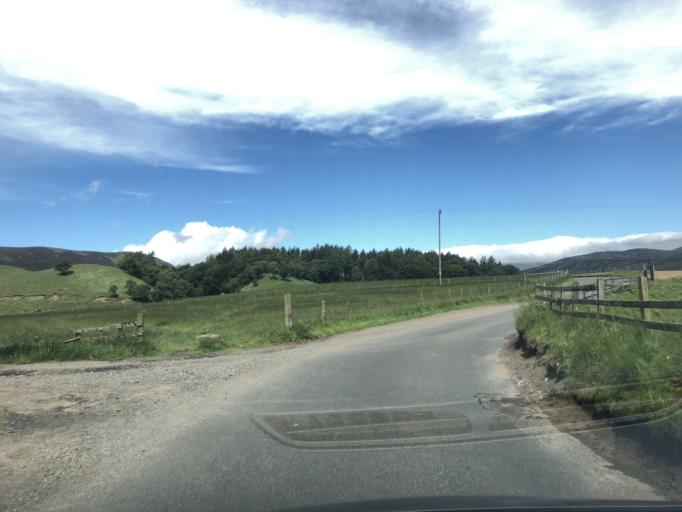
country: GB
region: Scotland
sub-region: Angus
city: Kirriemuir
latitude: 56.7605
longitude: -3.0193
